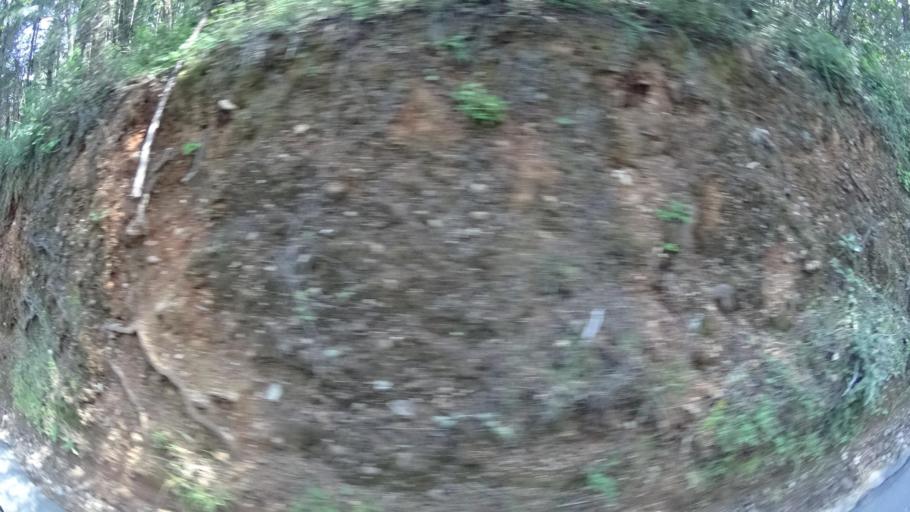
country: US
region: California
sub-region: Humboldt County
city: Redway
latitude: 40.1710
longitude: -123.6103
